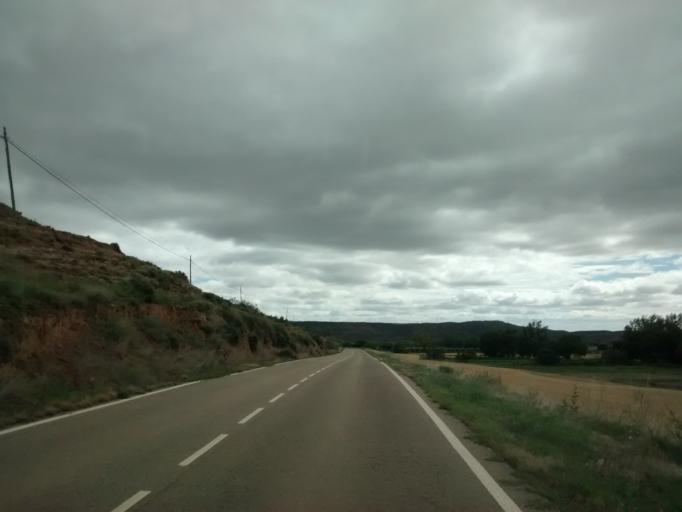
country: ES
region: Aragon
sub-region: Provincia de Zaragoza
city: Trasmoz
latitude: 41.8317
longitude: -1.7214
